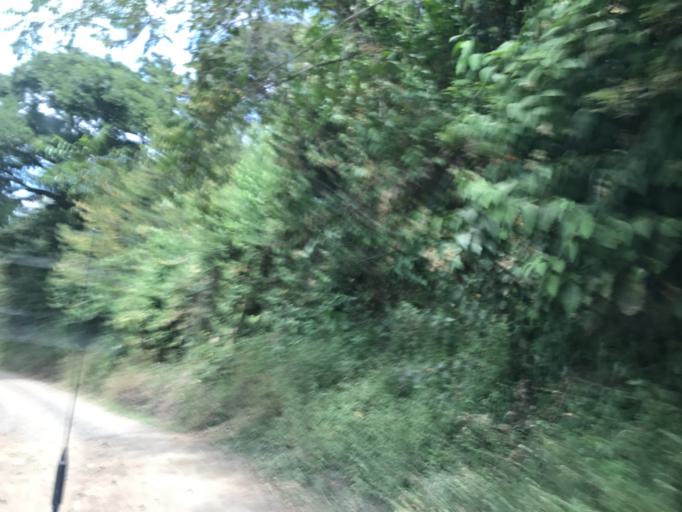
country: CO
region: Valle del Cauca
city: Obando
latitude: 4.5645
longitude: -75.9287
